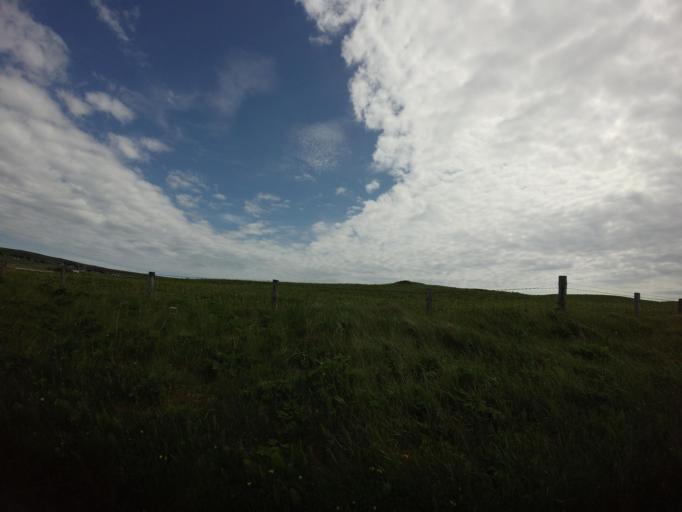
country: GB
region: Scotland
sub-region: Eilean Siar
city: Isle of Lewis
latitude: 58.2858
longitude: -6.2828
